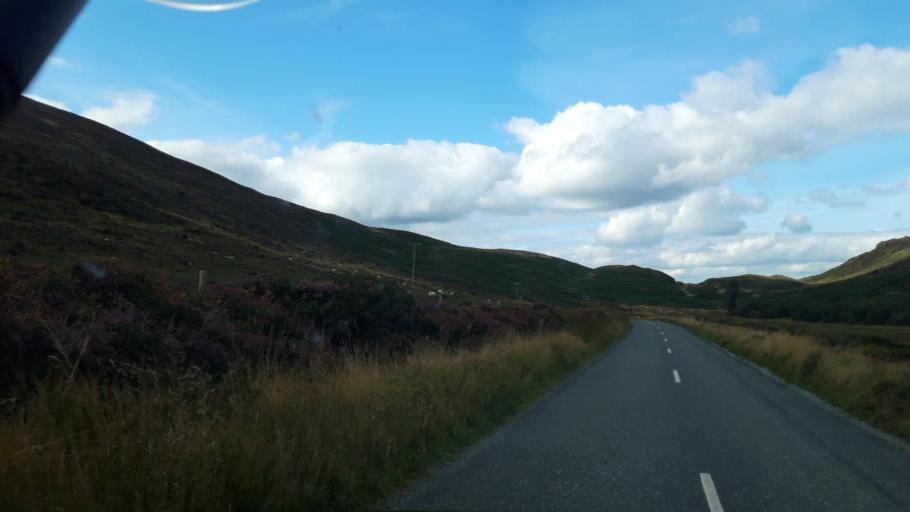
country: GB
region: Northern Ireland
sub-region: Down District
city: Warrenpoint
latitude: 54.0538
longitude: -6.2717
